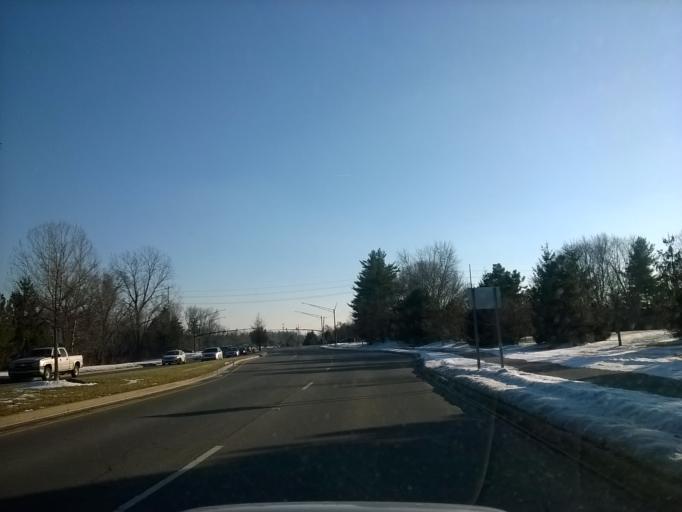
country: US
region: Indiana
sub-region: Hamilton County
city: Carmel
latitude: 39.9583
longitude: -86.0747
